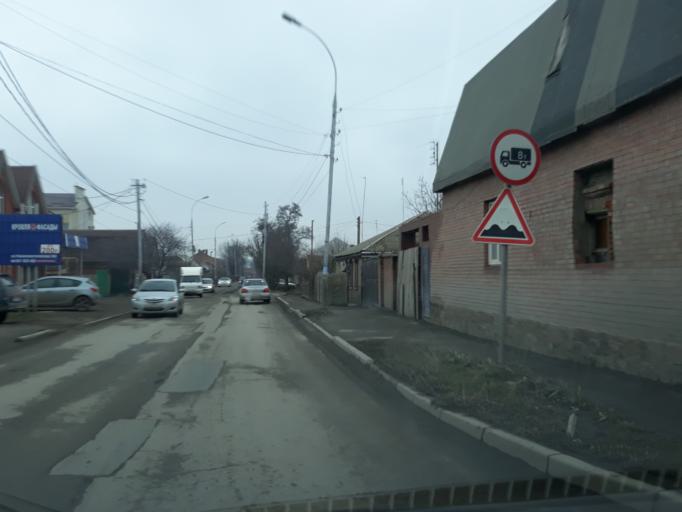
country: RU
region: Rostov
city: Taganrog
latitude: 47.2356
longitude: 38.9265
